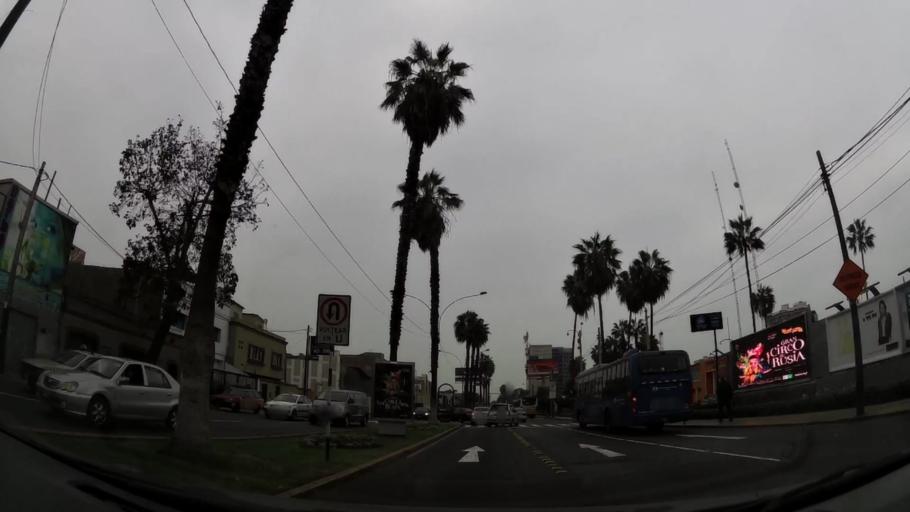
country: PE
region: Lima
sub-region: Lima
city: Surco
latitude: -12.1374
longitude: -77.0226
